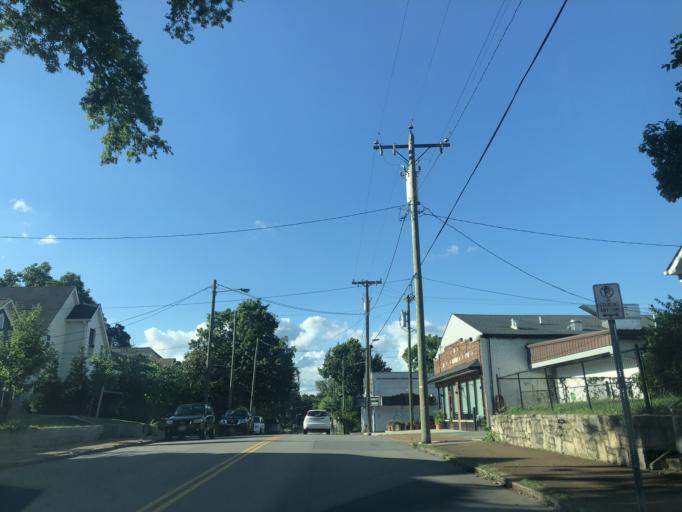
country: US
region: Tennessee
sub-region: Davidson County
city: Nashville
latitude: 36.1852
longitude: -86.7683
